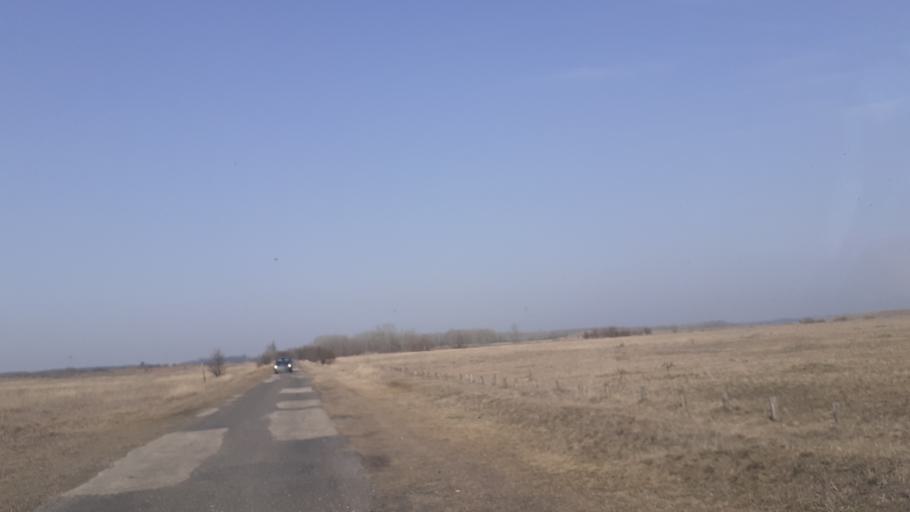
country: HU
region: Pest
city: Dabas
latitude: 47.1039
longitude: 19.2263
